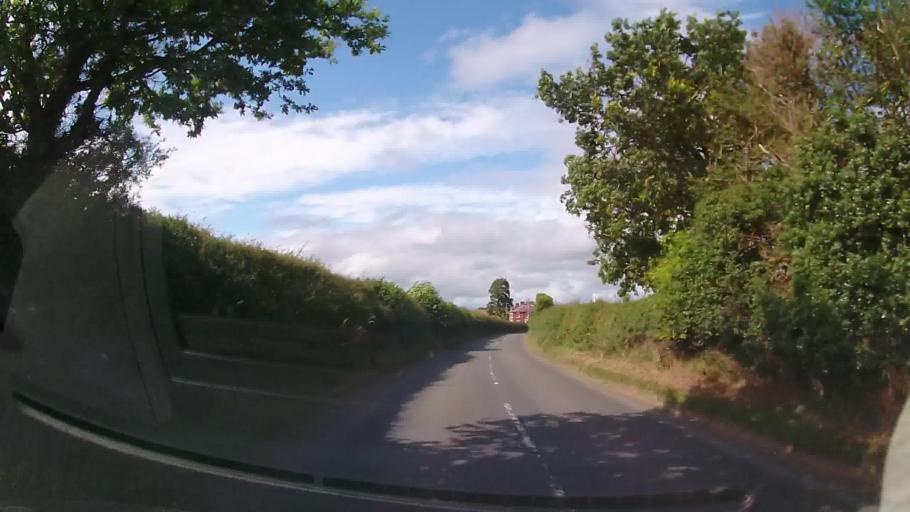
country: GB
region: England
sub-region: Shropshire
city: Petton
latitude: 52.8381
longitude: -2.8055
